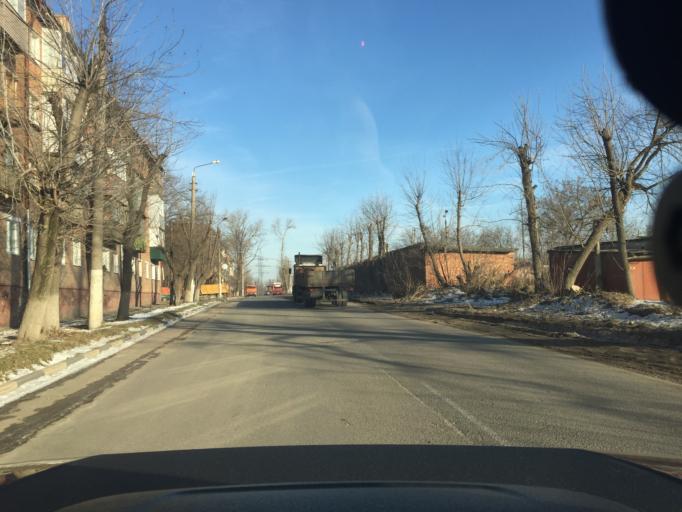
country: RU
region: Tula
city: Tula
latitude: 54.1773
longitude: 37.7087
